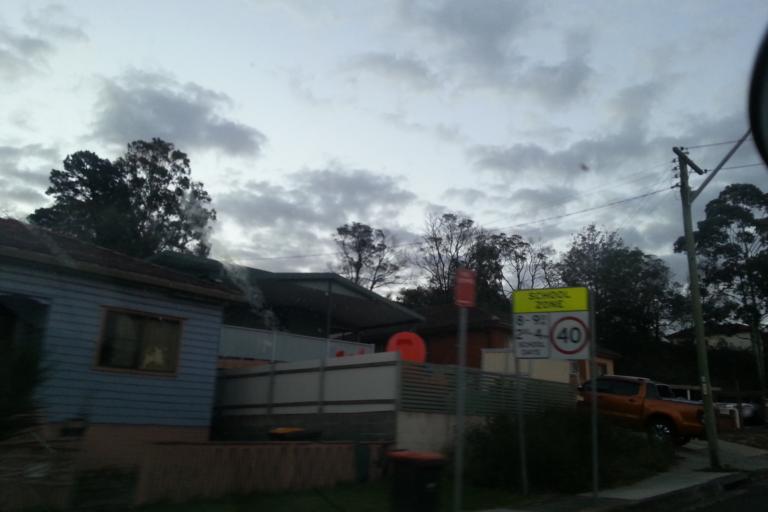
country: AU
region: New South Wales
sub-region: Wollongong
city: Cringila
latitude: -34.4718
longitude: 150.8713
